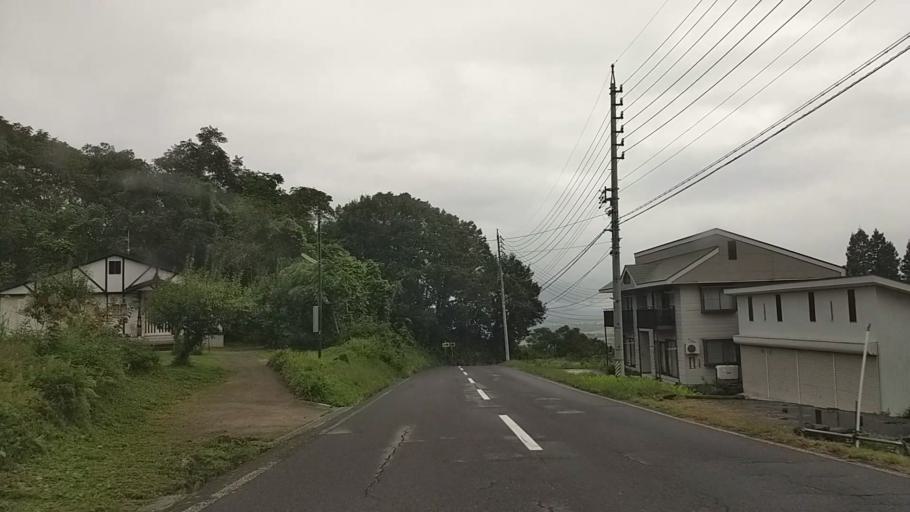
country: JP
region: Nagano
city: Iiyama
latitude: 36.8299
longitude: 138.4087
